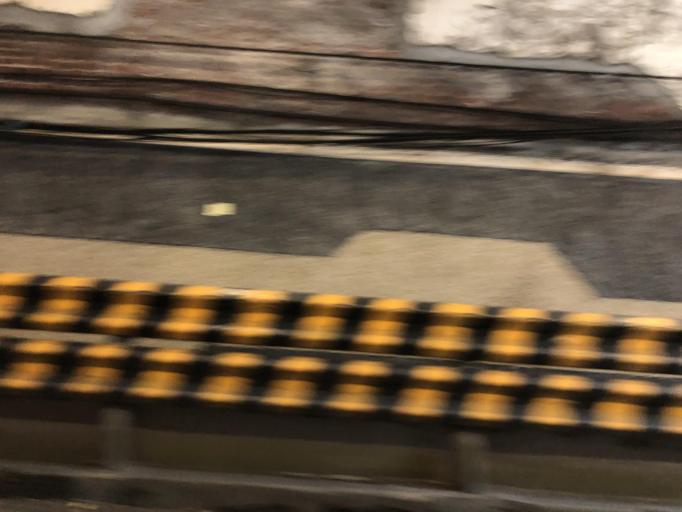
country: TW
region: Taiwan
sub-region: Keelung
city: Keelung
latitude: 25.1164
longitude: 121.7437
